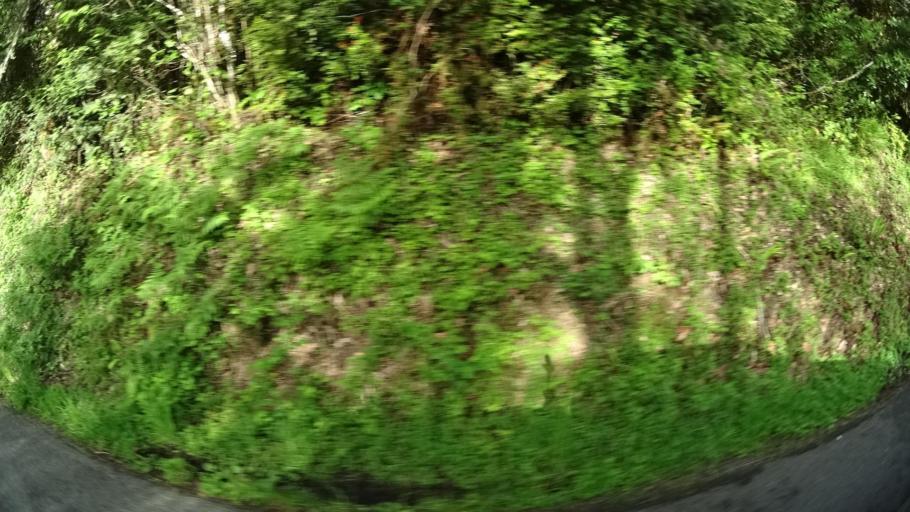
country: US
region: California
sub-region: Humboldt County
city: Blue Lake
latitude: 40.8810
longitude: -124.0170
